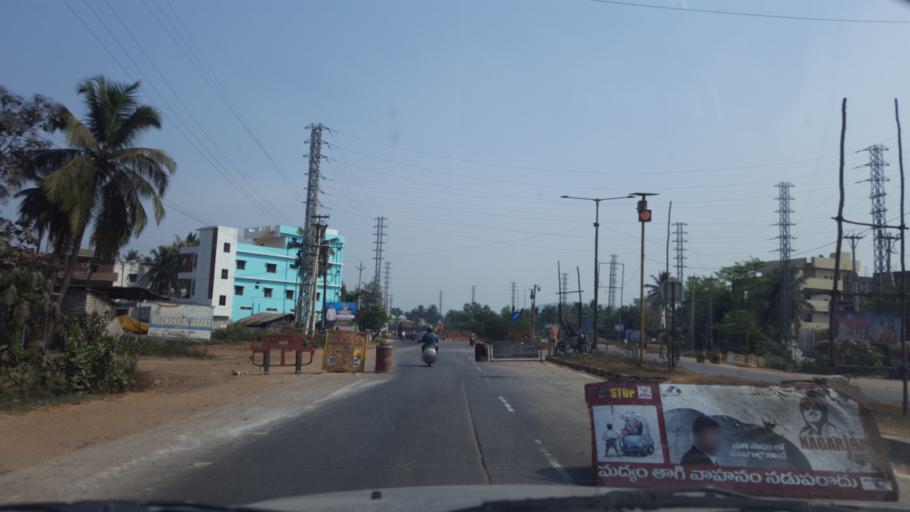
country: IN
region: Andhra Pradesh
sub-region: Vishakhapatnam
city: Anakapalle
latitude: 17.6766
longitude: 82.9957
